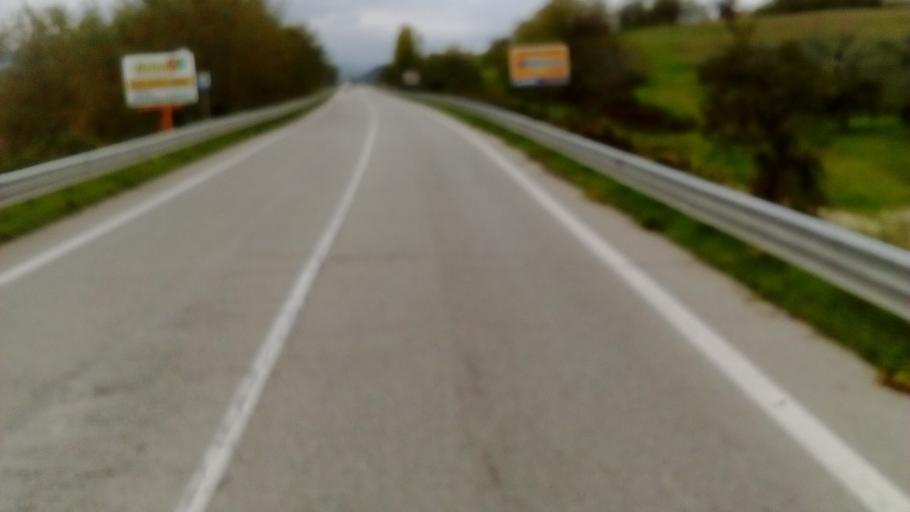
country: IT
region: Abruzzo
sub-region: Provincia di Chieti
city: San Salvo
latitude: 42.0206
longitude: 14.7302
